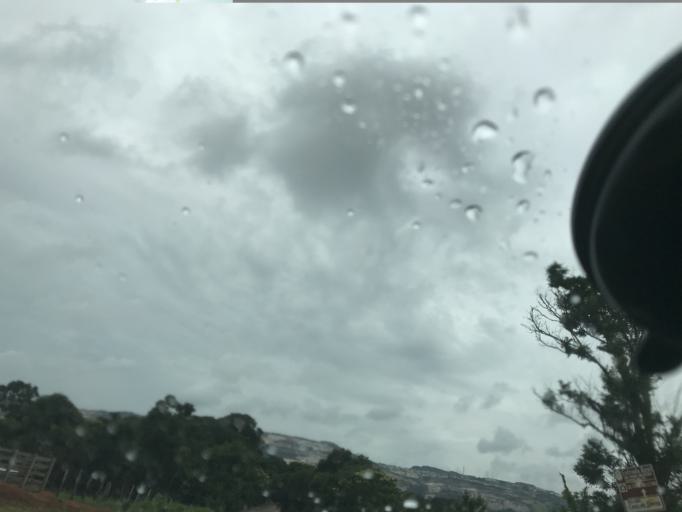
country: BR
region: Minas Gerais
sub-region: Conceicao Do Rio Verde
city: Conceicao do Rio Verde
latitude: -21.6939
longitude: -45.0043
